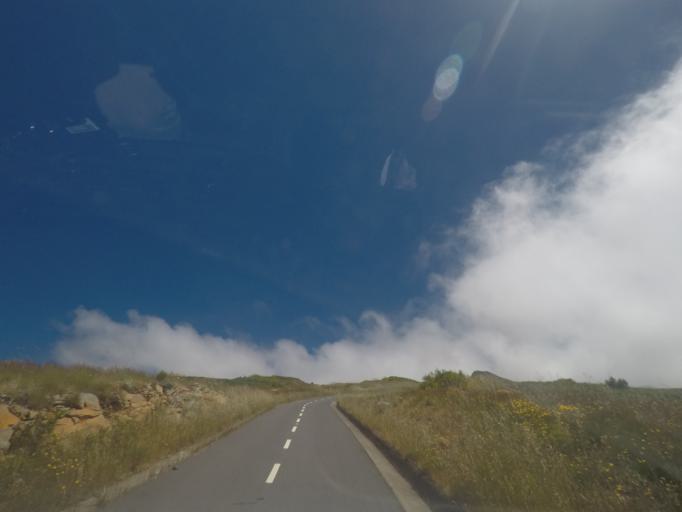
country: PT
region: Madeira
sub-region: Camara de Lobos
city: Curral das Freiras
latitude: 32.7115
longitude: -16.9385
